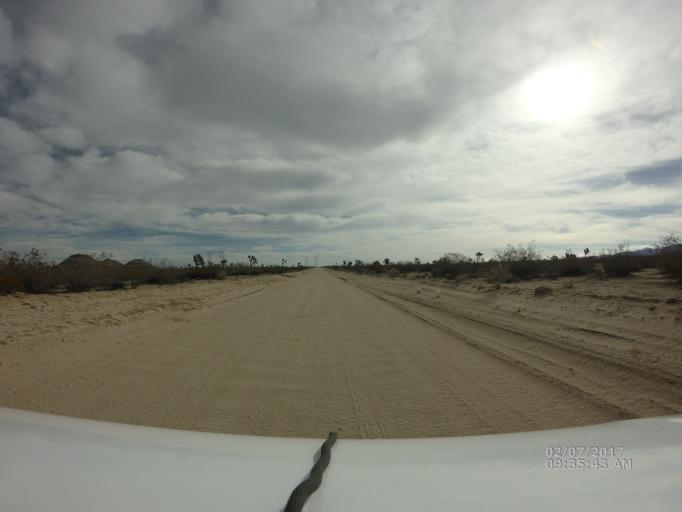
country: US
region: California
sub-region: San Bernardino County
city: Pinon Hills
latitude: 34.5276
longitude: -117.7206
